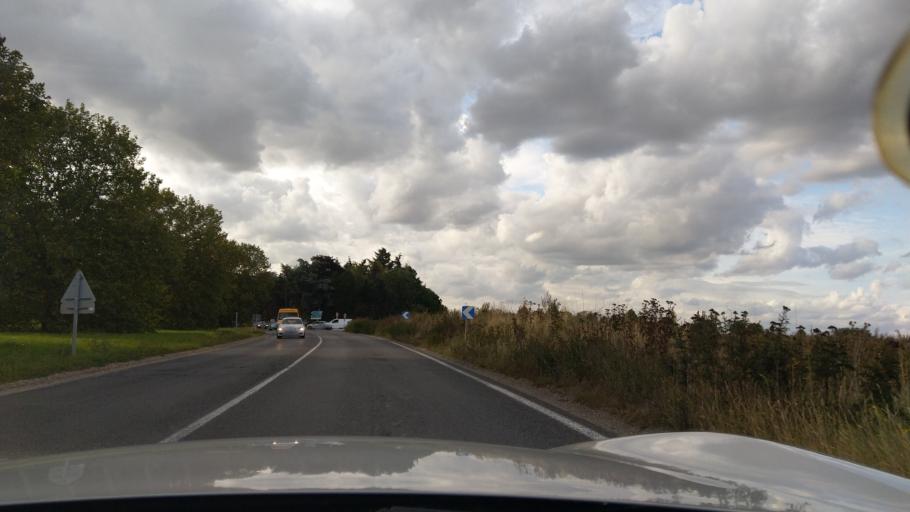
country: FR
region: Ile-de-France
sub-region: Departement de Seine-et-Marne
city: Mitry-Mory
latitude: 49.0132
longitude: 2.6046
